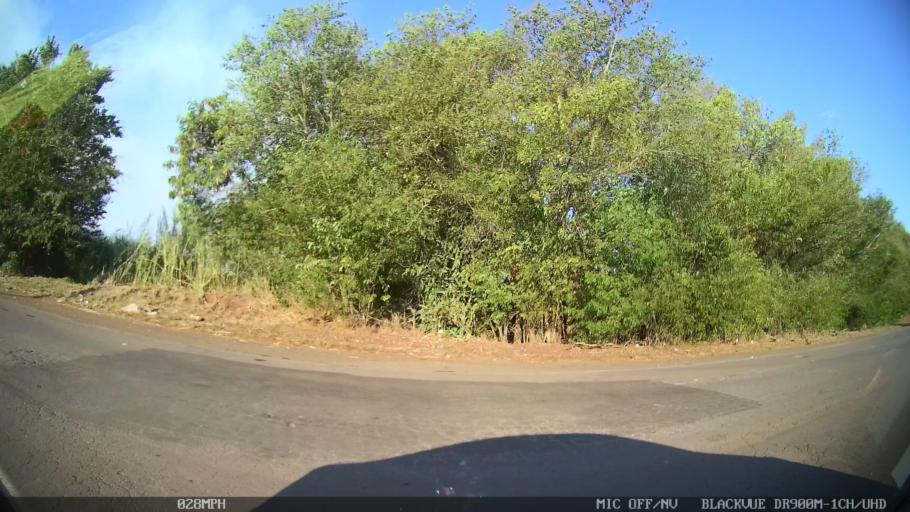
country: BR
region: Sao Paulo
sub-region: Piracicaba
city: Piracicaba
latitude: -22.6970
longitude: -47.6011
